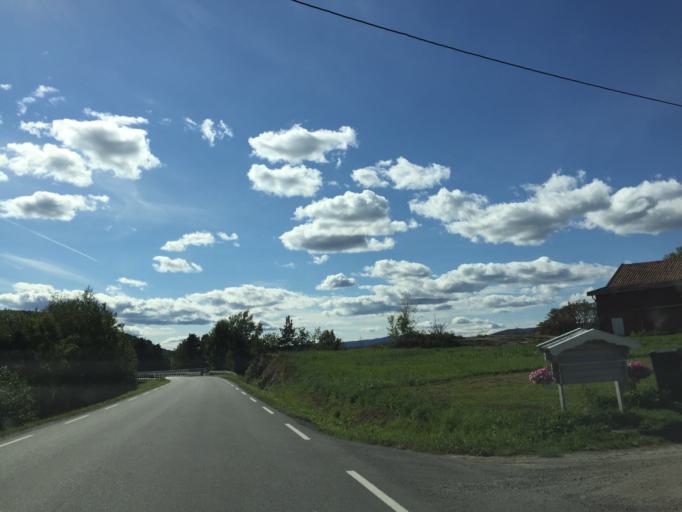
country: NO
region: Buskerud
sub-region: Ovre Eiker
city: Hokksund
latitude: 59.7012
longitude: 9.8471
